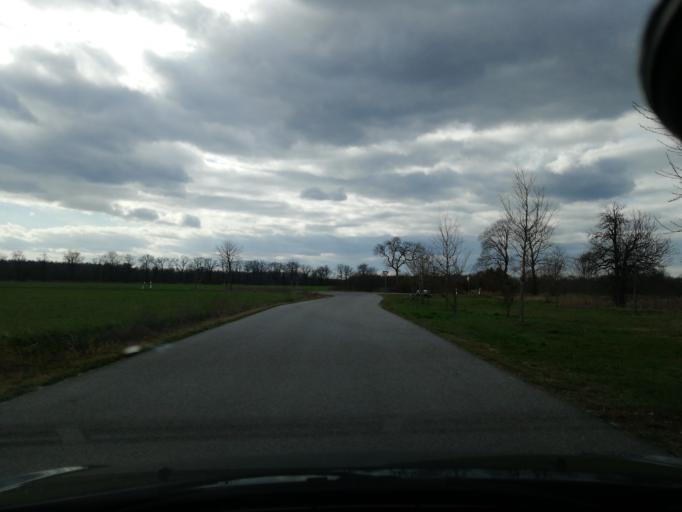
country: DE
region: Brandenburg
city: Altdobern
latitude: 51.6901
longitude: 14.1016
